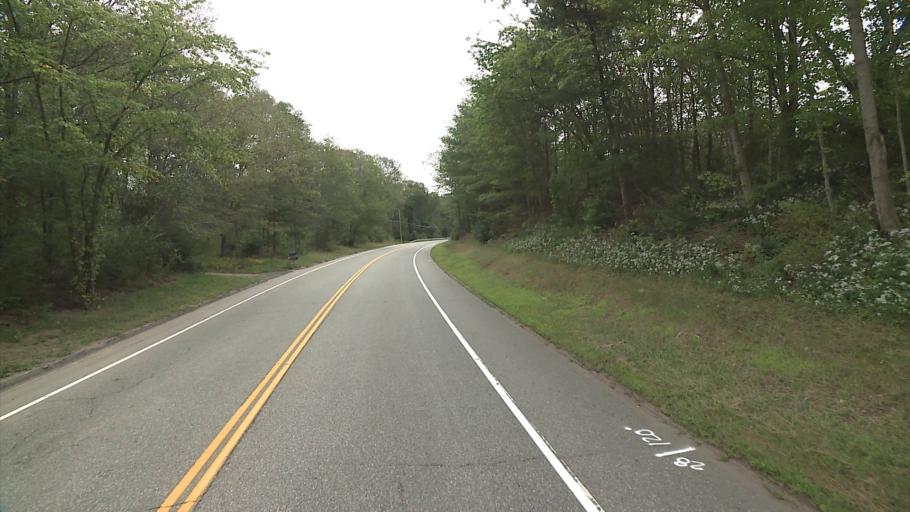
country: US
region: Connecticut
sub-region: Tolland County
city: Hebron
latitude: 41.6753
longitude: -72.3997
